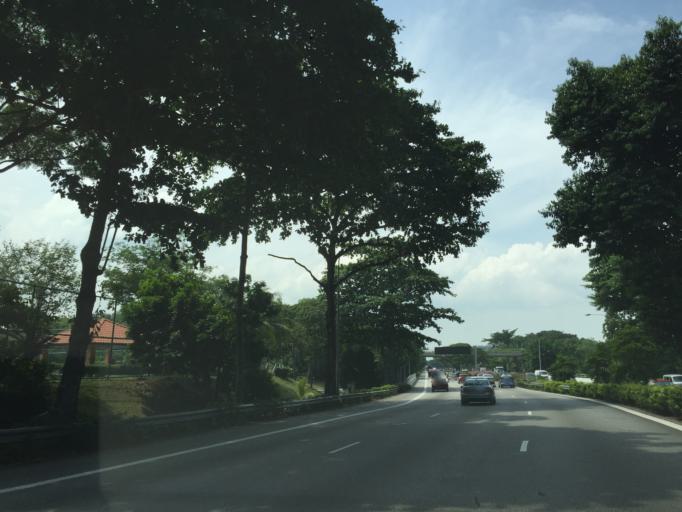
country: SG
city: Singapore
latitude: 1.3354
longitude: 103.9393
